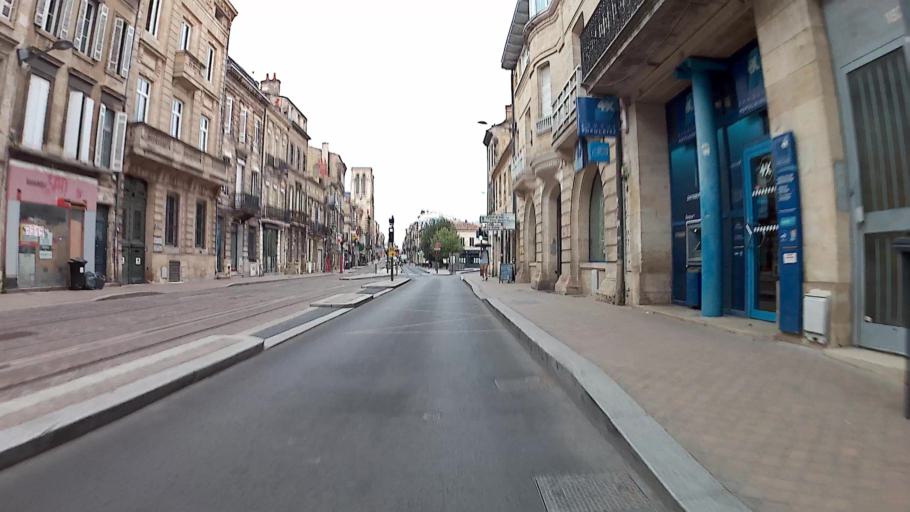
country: FR
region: Aquitaine
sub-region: Departement de la Gironde
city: Bordeaux
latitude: 44.8496
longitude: -0.5850
